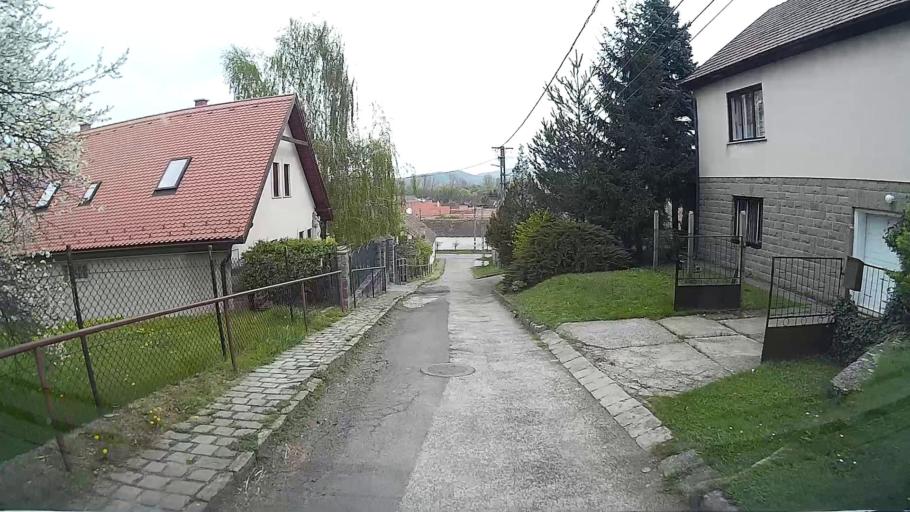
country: HU
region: Pest
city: Dunabogdany
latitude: 47.7908
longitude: 19.0344
